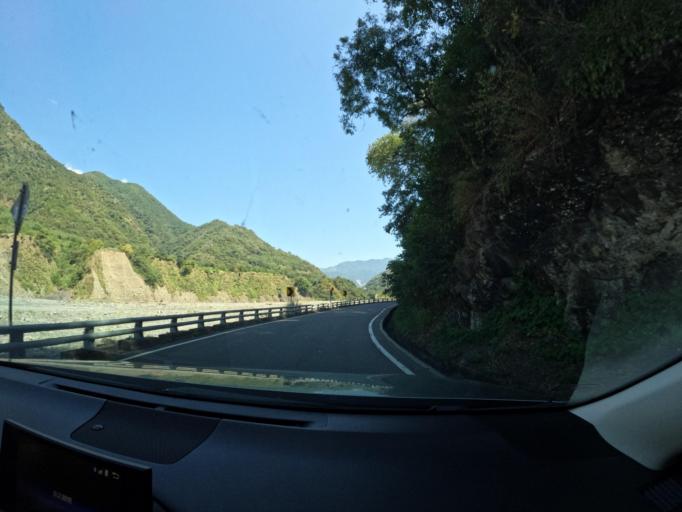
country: TW
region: Taiwan
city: Yujing
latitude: 23.2252
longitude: 120.8051
